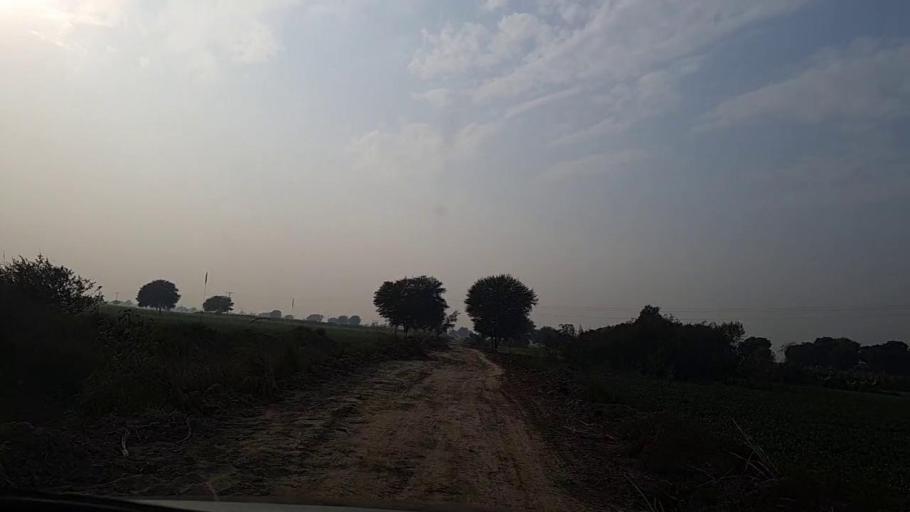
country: PK
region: Sindh
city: Nawabshah
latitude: 26.2695
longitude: 68.3215
